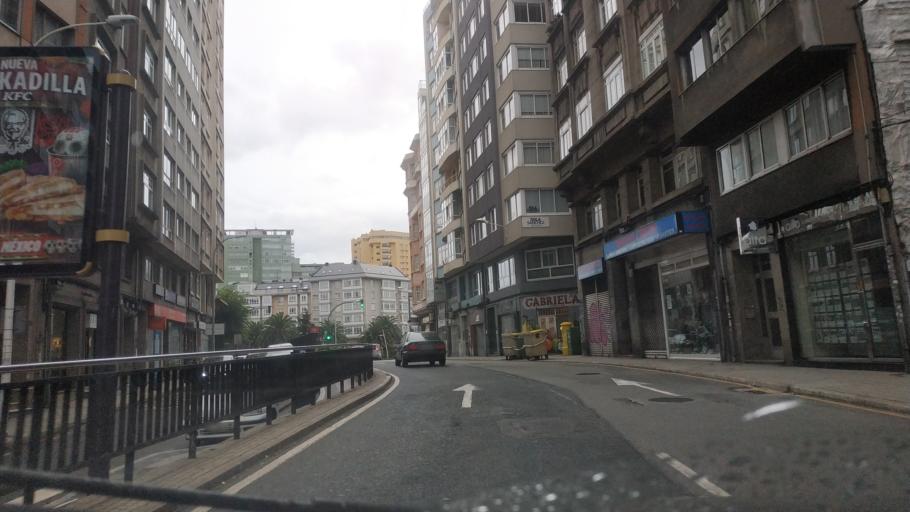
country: ES
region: Galicia
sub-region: Provincia da Coruna
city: A Coruna
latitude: 43.3600
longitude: -8.4061
